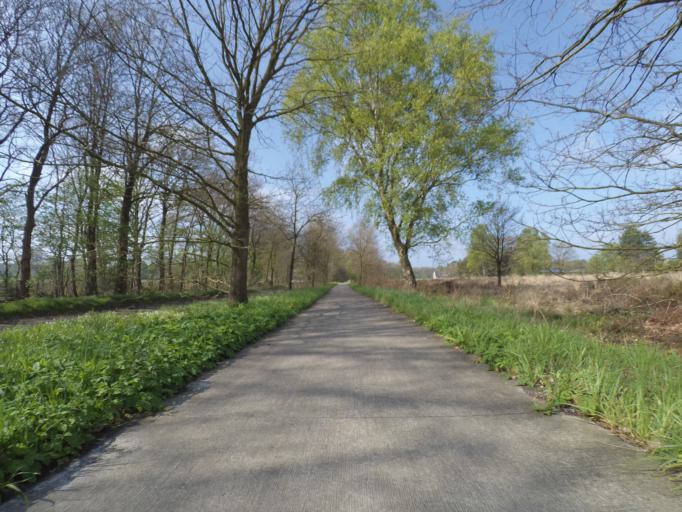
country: NL
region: Gelderland
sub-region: Gemeente Apeldoorn
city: Uddel
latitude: 52.2835
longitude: 5.7628
